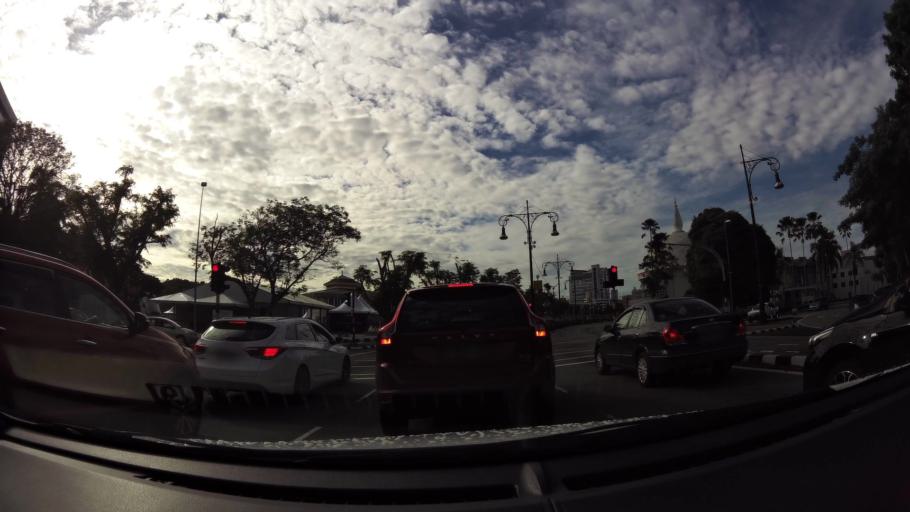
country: BN
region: Brunei and Muara
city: Bandar Seri Begawan
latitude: 4.8941
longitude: 114.9410
